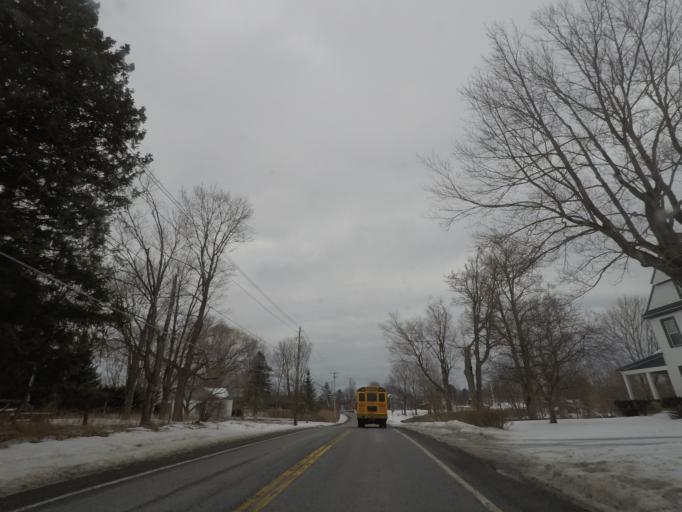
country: US
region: New York
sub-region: Saratoga County
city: Stillwater
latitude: 42.9437
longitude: -73.6622
